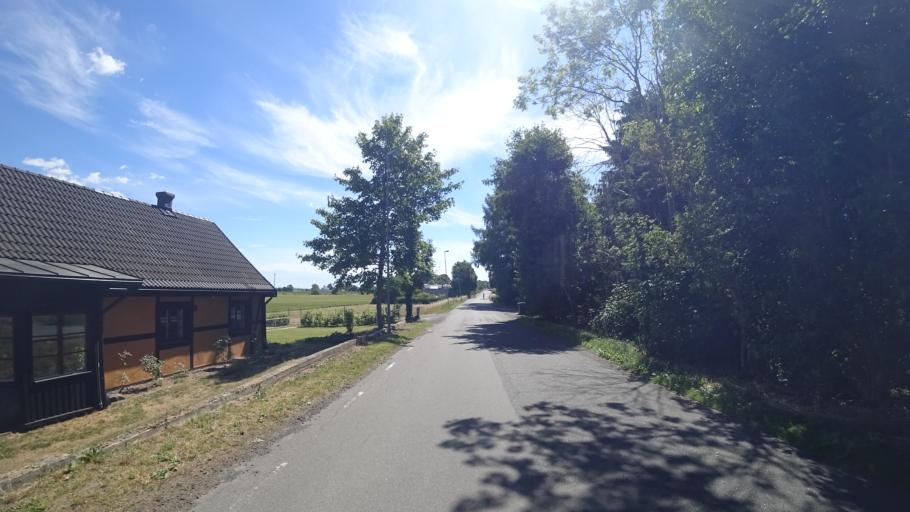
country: SE
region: Skane
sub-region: Kristianstads Kommun
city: Onnestad
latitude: 56.0471
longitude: 14.0268
